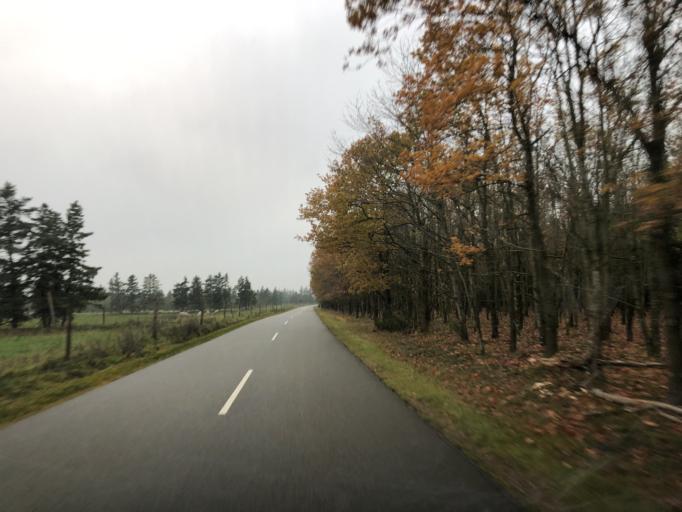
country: DK
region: Central Jutland
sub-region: Herning Kommune
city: Sunds
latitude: 56.2236
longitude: 8.9270
